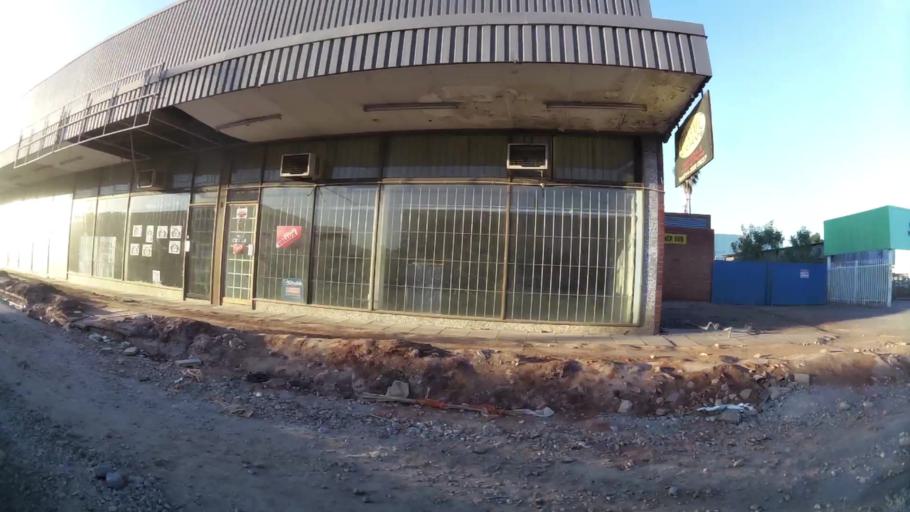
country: ZA
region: North-West
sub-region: Bojanala Platinum District Municipality
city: Rustenburg
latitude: -25.6660
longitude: 27.2428
